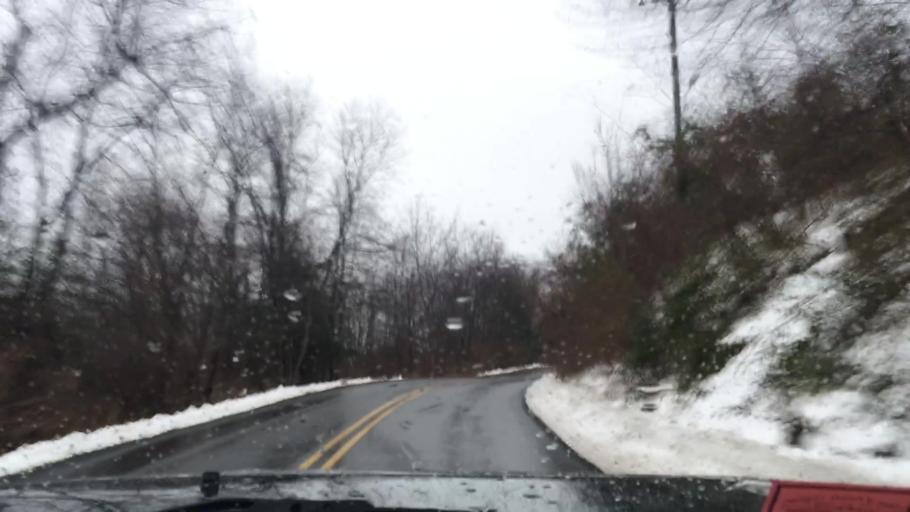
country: US
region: Virginia
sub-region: Pulaski County
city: Dublin
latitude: 37.0188
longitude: -80.6301
